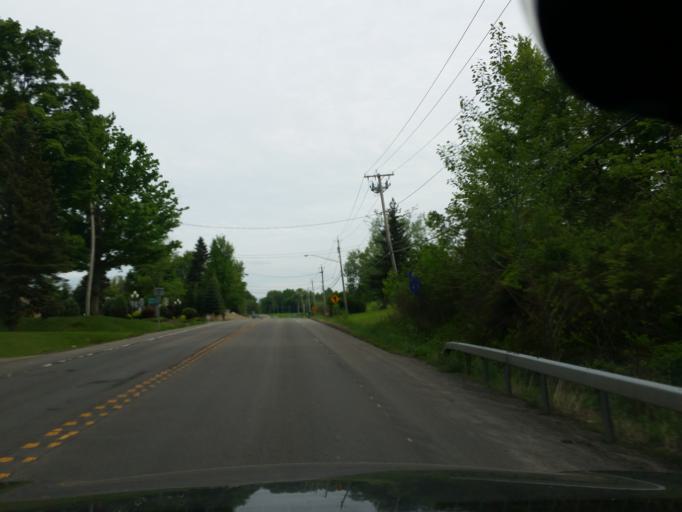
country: US
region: New York
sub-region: Chautauqua County
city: Lakewood
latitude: 42.1142
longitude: -79.3873
